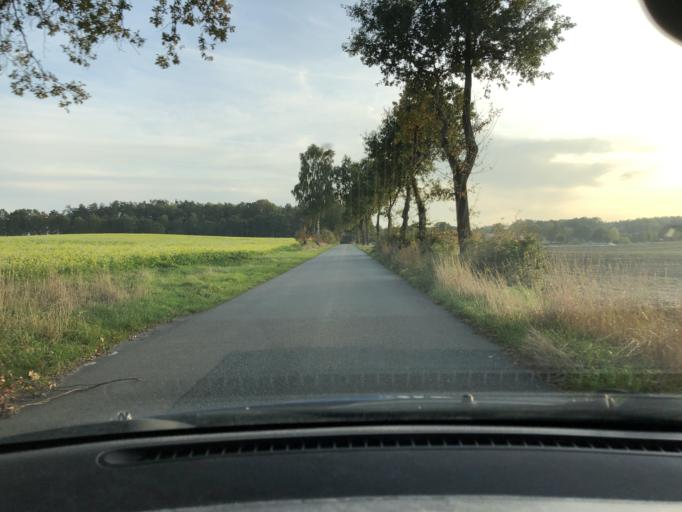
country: DE
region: Lower Saxony
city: Gohrde
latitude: 53.1280
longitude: 10.9456
